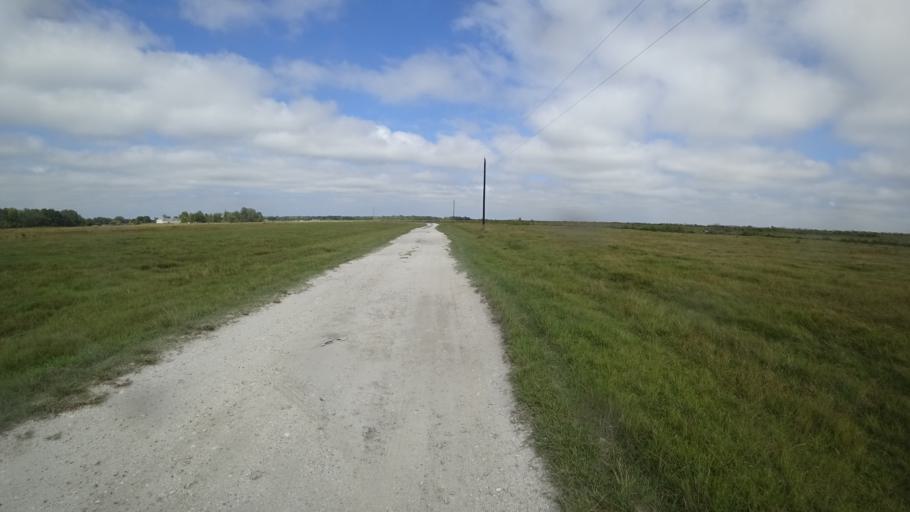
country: US
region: Florida
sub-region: DeSoto County
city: Arcadia
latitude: 27.3195
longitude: -82.1099
